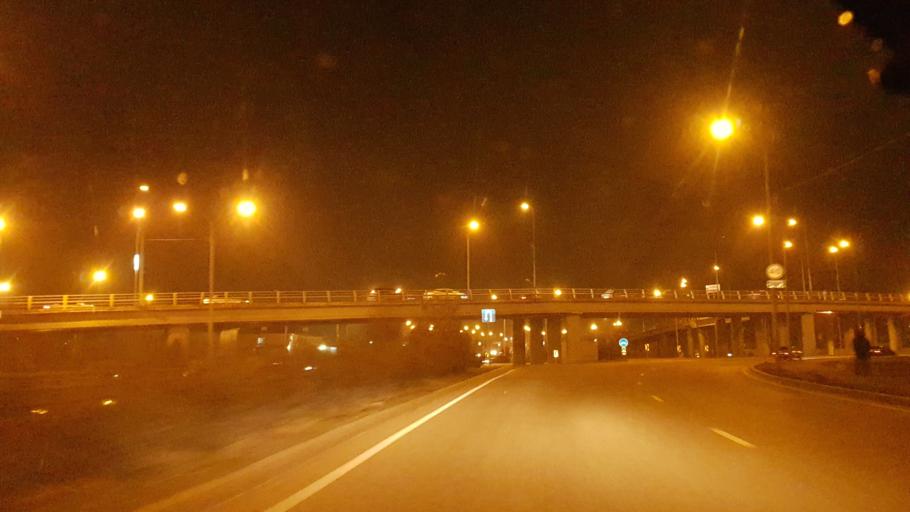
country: KZ
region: Almaty Qalasy
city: Almaty
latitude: 43.2733
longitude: 76.8862
